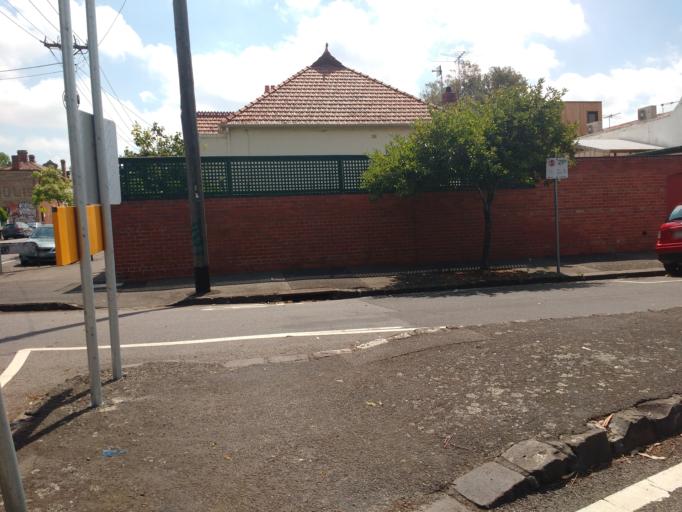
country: AU
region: Victoria
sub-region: Yarra
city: North Fitzroy
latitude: -37.7847
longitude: 144.9739
